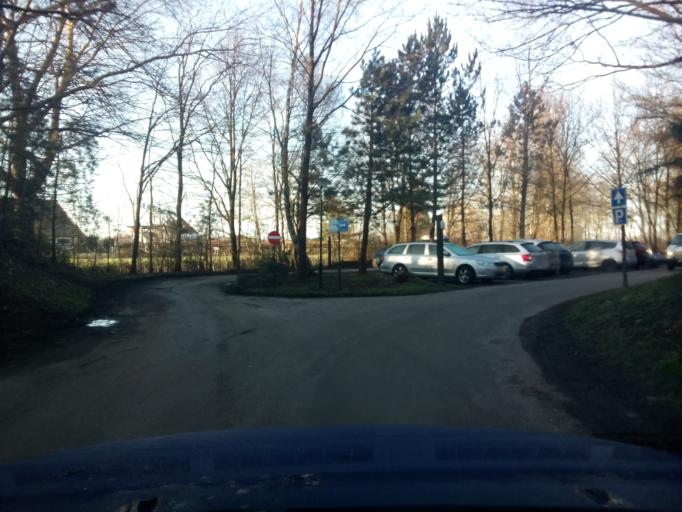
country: NL
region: Drenthe
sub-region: Gemeente Coevorden
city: Dalen
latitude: 52.6728
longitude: 6.7785
